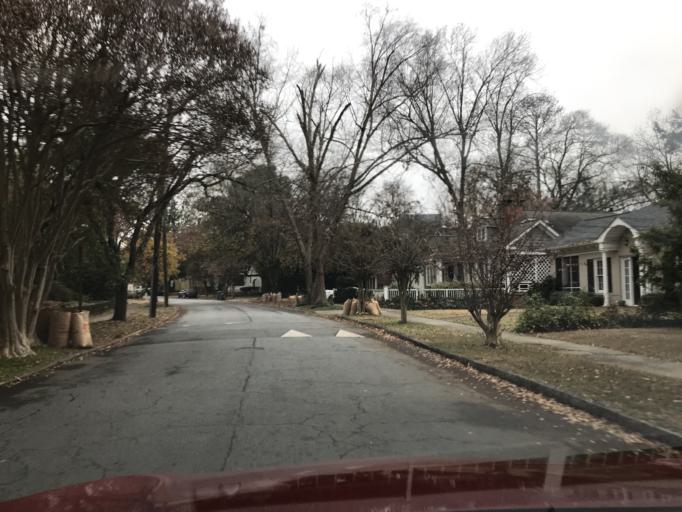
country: US
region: Georgia
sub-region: Fulton County
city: Atlanta
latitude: 33.8000
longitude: -84.3946
